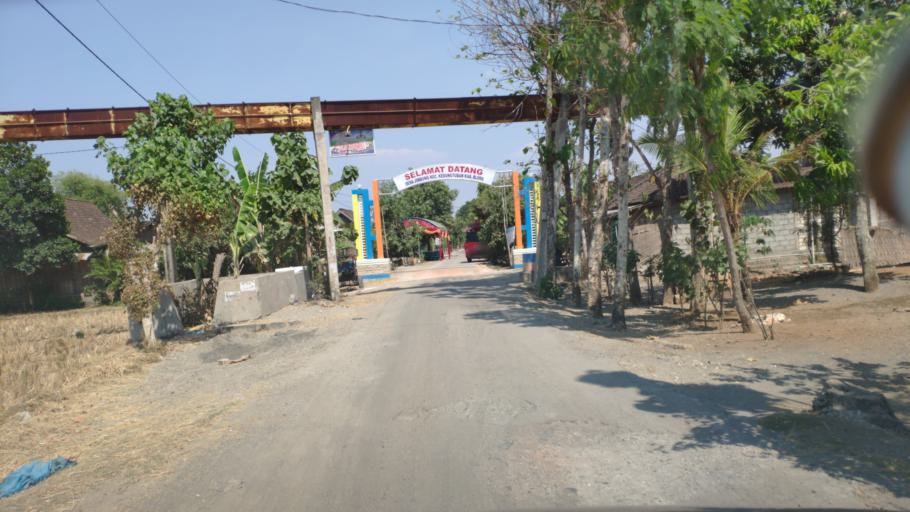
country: ID
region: Central Java
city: Ketuwan
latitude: -7.2362
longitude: 111.5144
